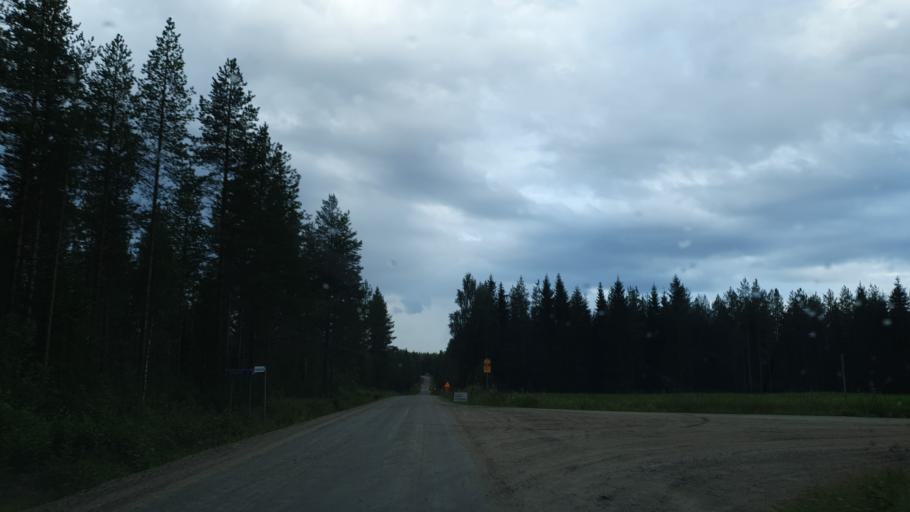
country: FI
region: Kainuu
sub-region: Kehys-Kainuu
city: Kuhmo
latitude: 64.2118
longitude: 29.3694
